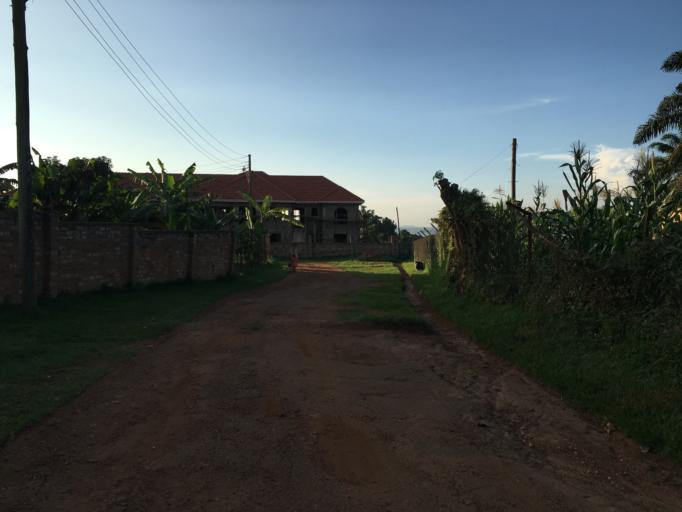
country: UG
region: Central Region
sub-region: Wakiso District
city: Entebbe
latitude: 0.0509
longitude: 32.4630
